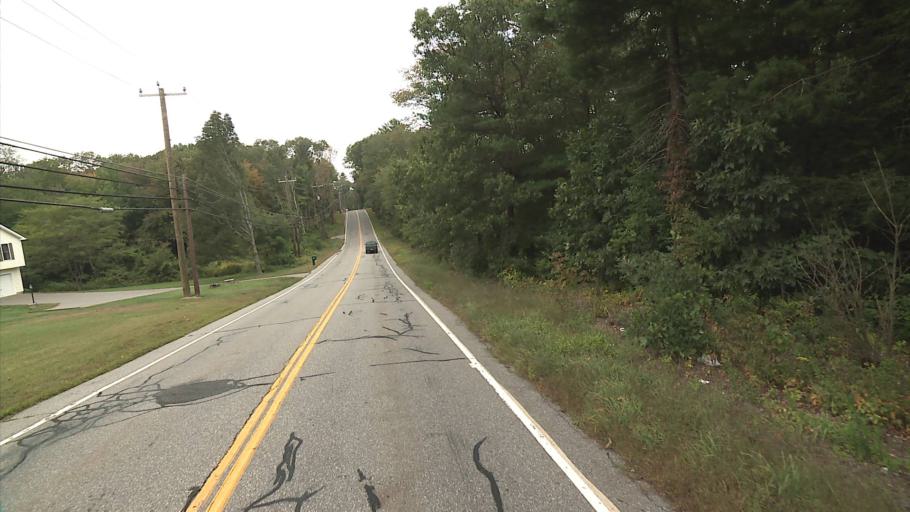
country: US
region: Connecticut
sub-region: Tolland County
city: Storrs
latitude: 41.8367
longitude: -72.2702
